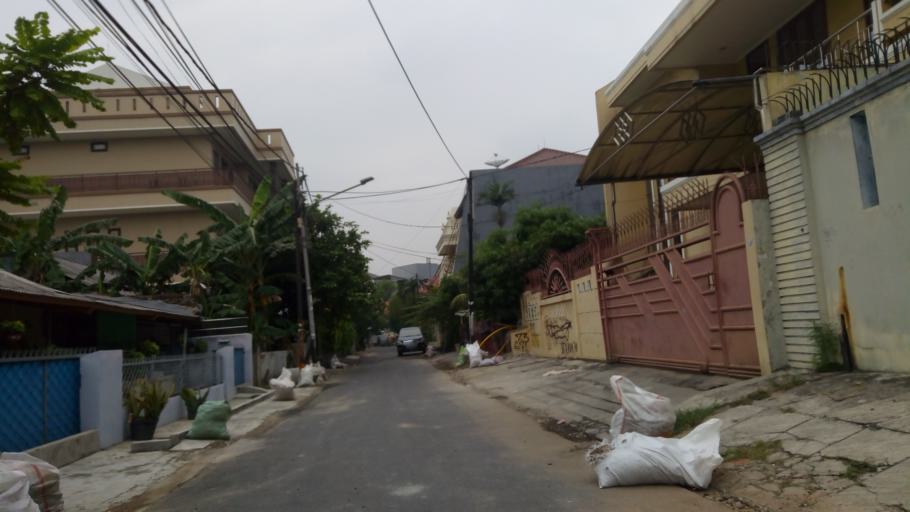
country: ID
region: Jakarta Raya
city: Jakarta
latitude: -6.1444
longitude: 106.8399
